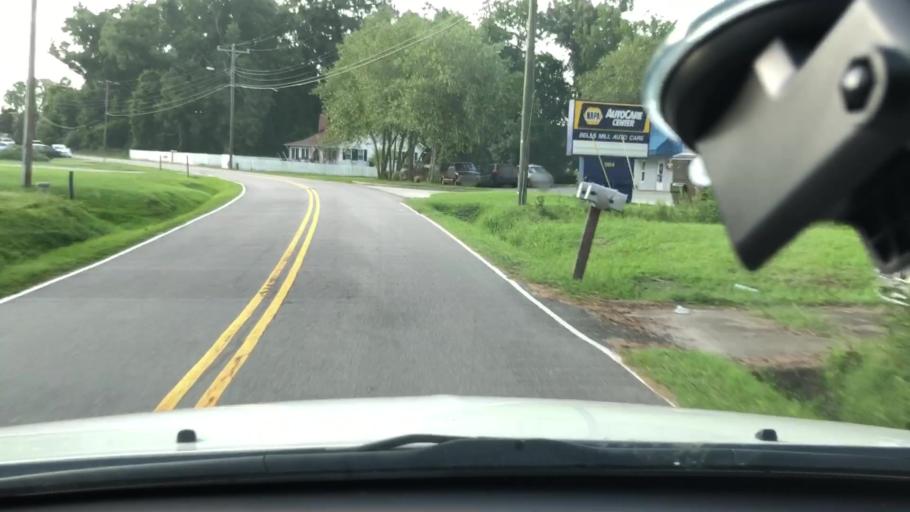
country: US
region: Virginia
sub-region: City of Chesapeake
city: Chesapeake
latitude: 36.7209
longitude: -76.2670
